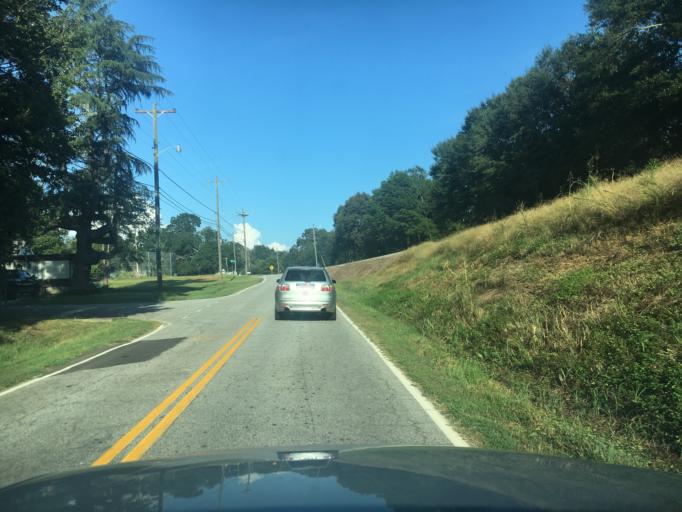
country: US
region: South Carolina
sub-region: Oconee County
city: Westminster
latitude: 34.6609
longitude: -83.0861
